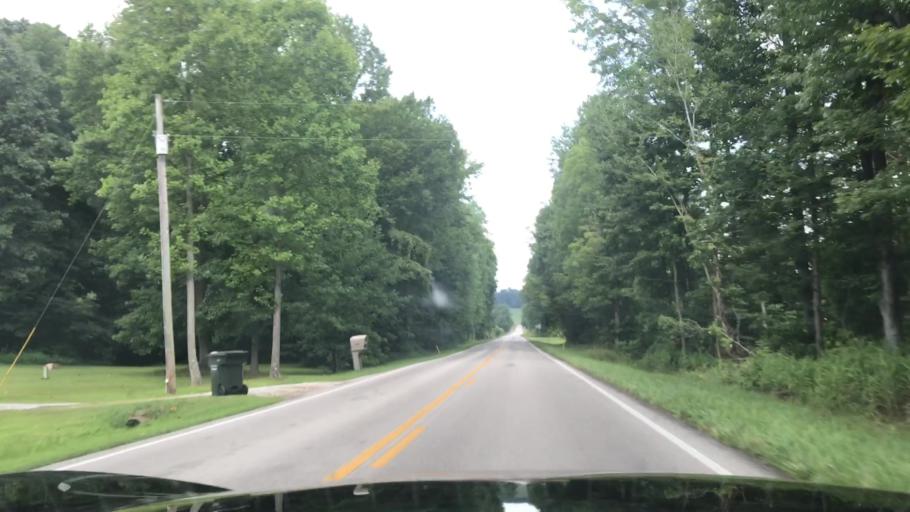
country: US
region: Kentucky
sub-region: Butler County
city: Morgantown
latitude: 37.1750
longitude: -86.8406
